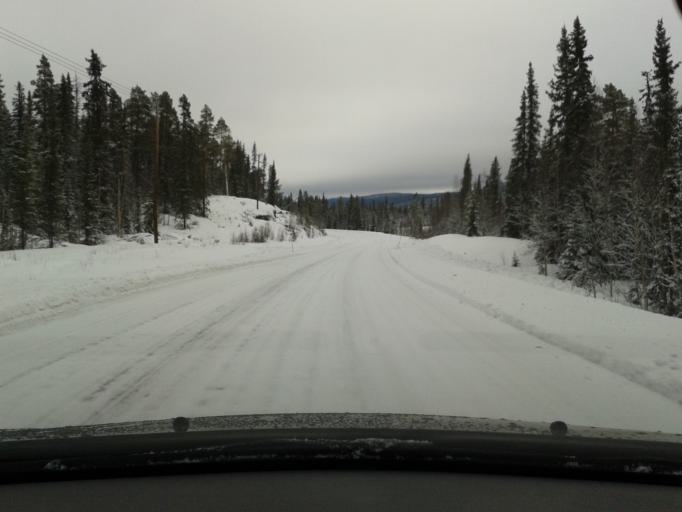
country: SE
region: Vaesterbotten
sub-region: Vilhelmina Kommun
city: Sjoberg
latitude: 65.2360
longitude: 15.8353
